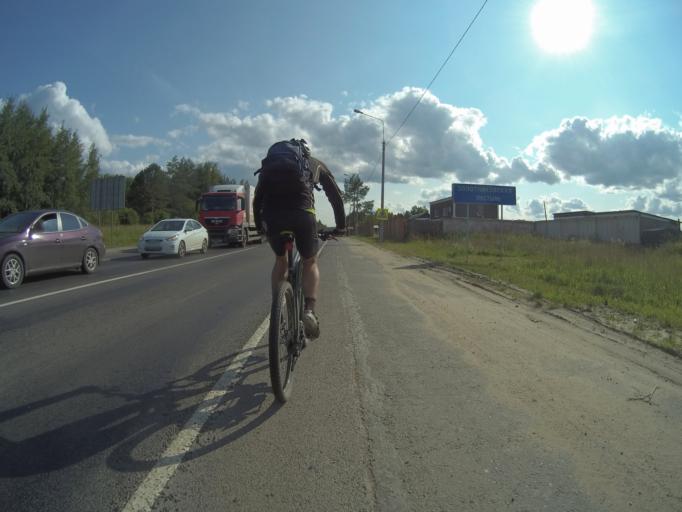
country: RU
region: Ivanovo
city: Novoye Leushino
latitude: 56.6912
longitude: 40.6198
